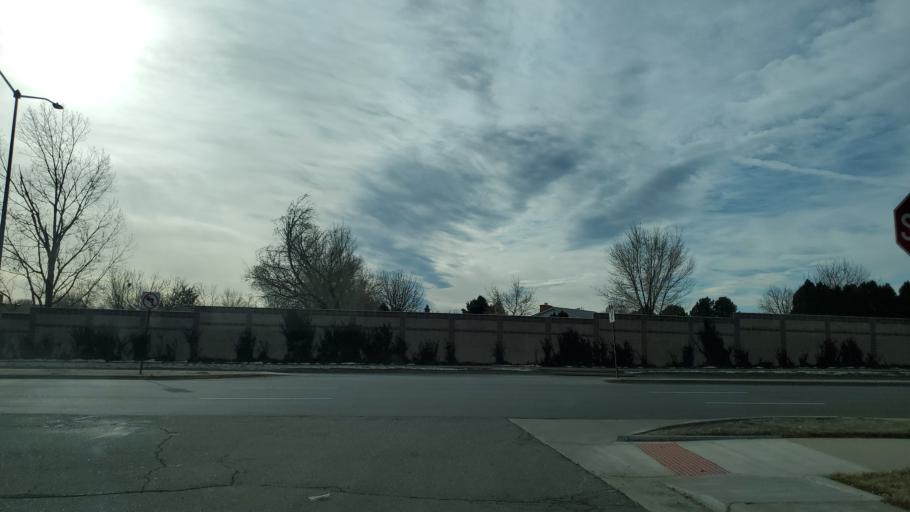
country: US
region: Colorado
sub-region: Adams County
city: Northglenn
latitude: 39.9141
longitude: -104.9497
